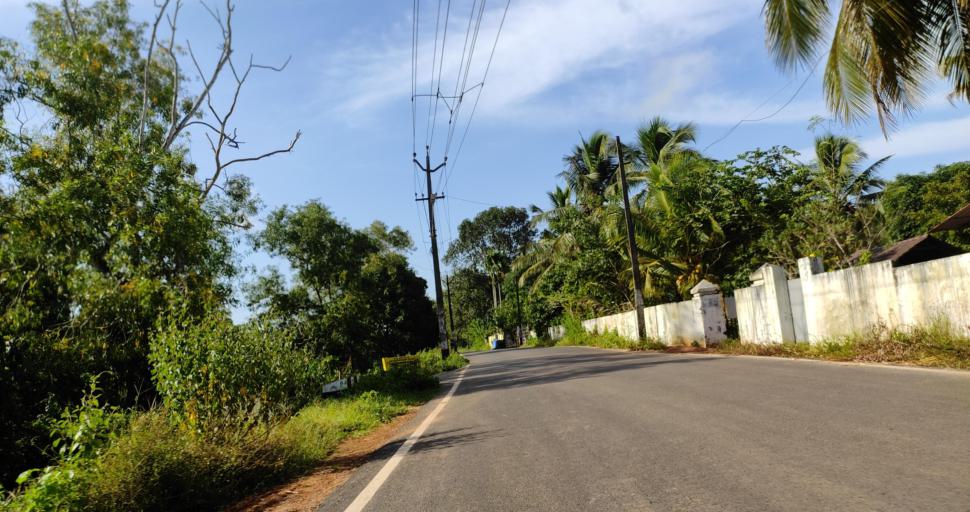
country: IN
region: Kerala
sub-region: Alappuzha
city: Shertallai
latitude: 9.6031
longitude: 76.3336
